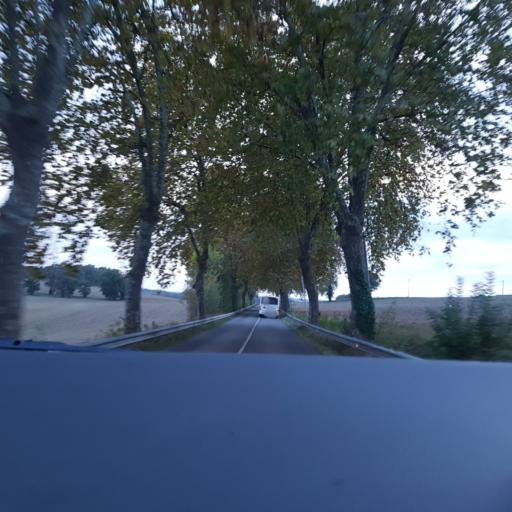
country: FR
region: Midi-Pyrenees
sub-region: Departement du Gers
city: Condom
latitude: 43.9489
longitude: 0.3307
